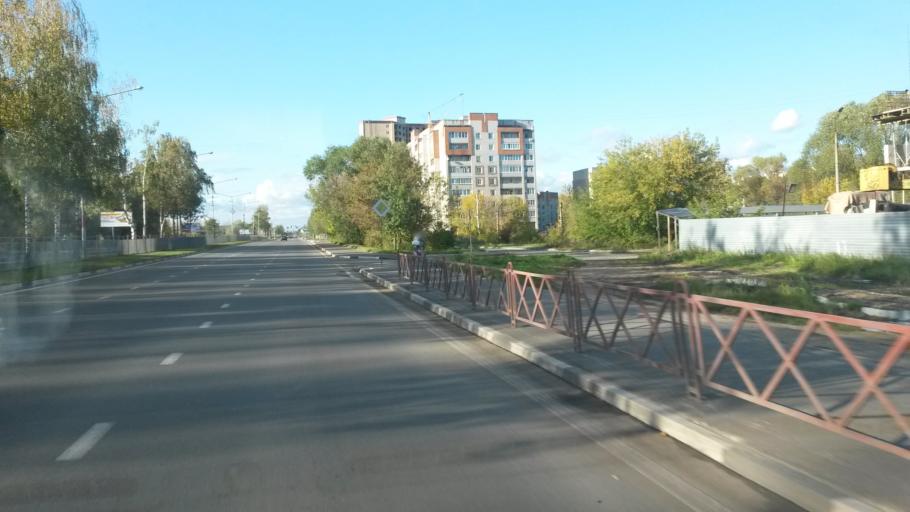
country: RU
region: Jaroslavl
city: Yaroslavl
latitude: 57.5623
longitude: 39.9340
